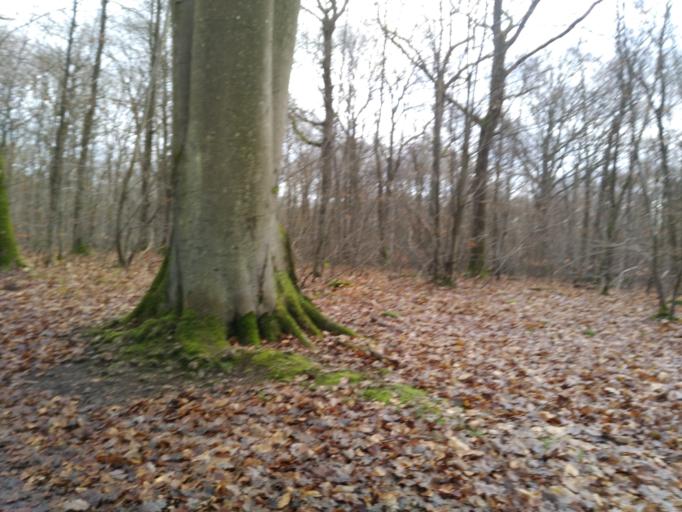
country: FR
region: Ile-de-France
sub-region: Departement des Yvelines
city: Neauphle-le-Chateau
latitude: 48.8058
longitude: 1.9306
